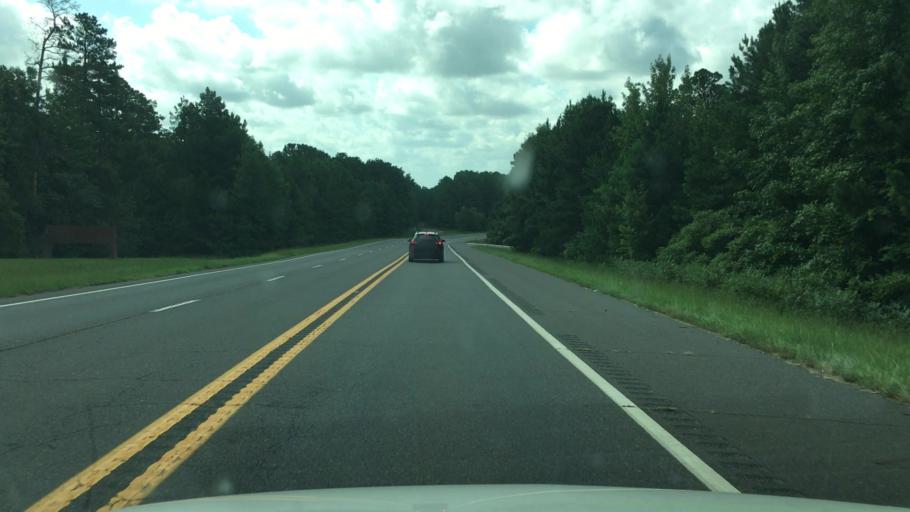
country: US
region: Arkansas
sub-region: Clark County
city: Arkadelphia
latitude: 34.2114
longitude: -93.0812
